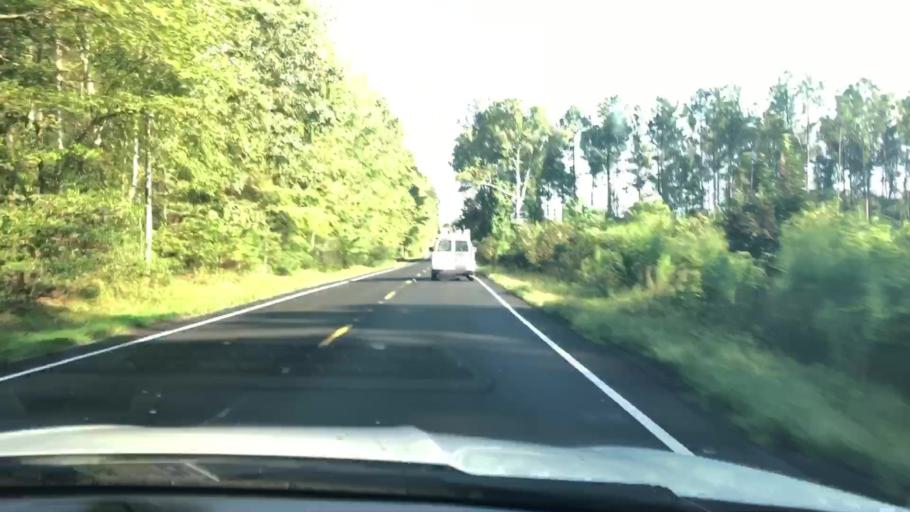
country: US
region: Virginia
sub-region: King William County
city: West Point
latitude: 37.4705
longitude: -76.8446
